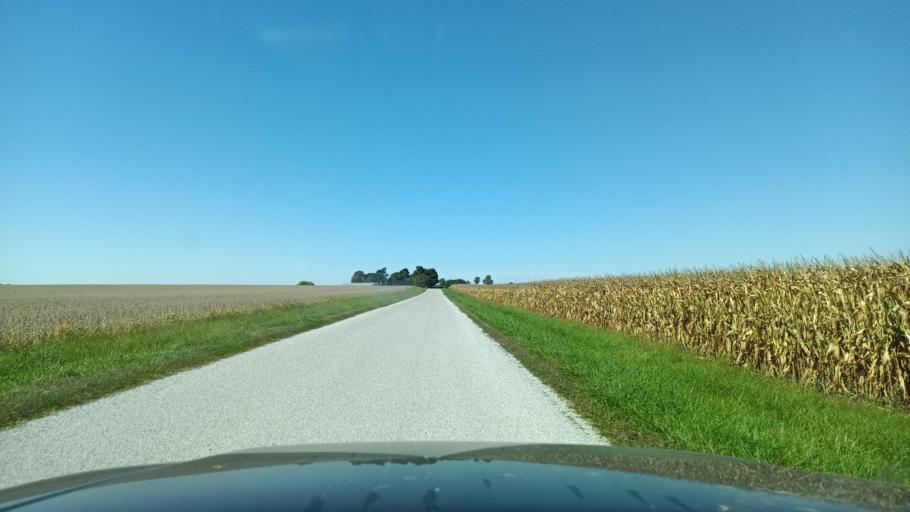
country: US
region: Illinois
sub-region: Champaign County
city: Mahomet
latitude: 40.0986
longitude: -88.4369
